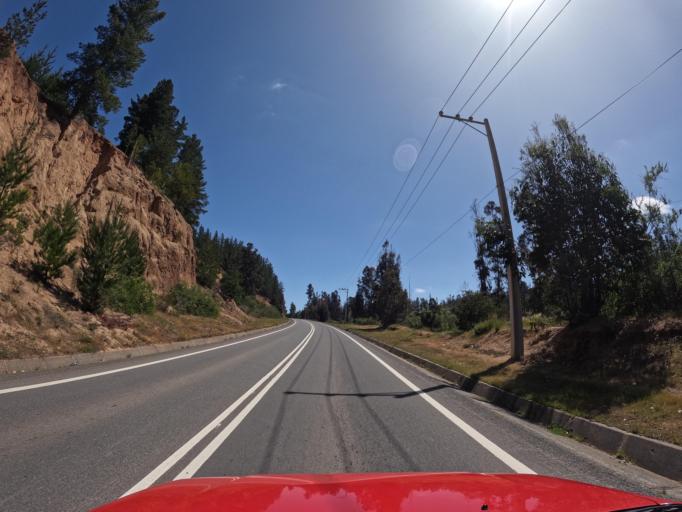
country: CL
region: O'Higgins
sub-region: Provincia de Colchagua
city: Santa Cruz
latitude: -34.6823
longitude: -71.7890
